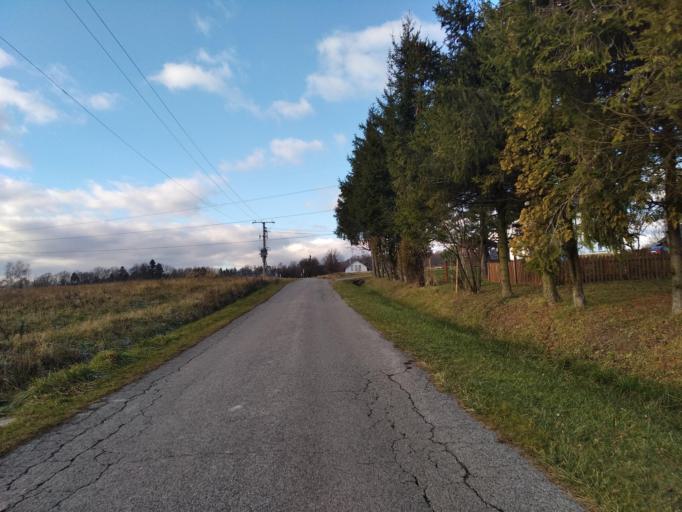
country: PL
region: Subcarpathian Voivodeship
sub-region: Powiat strzyzowski
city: Babica
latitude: 49.9449
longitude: 21.8783
